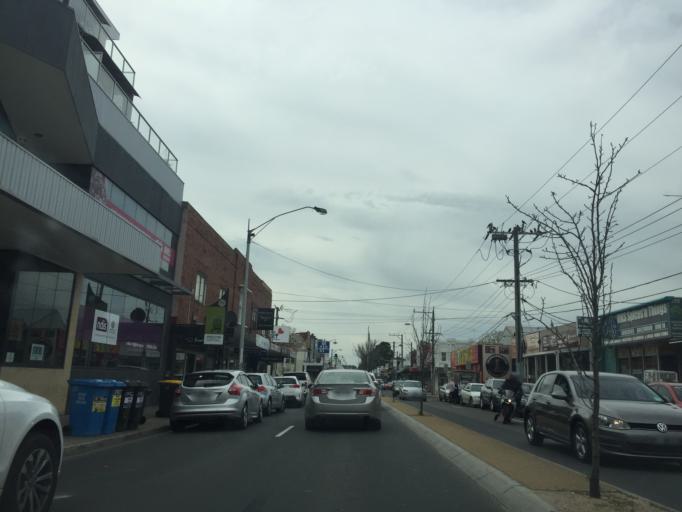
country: AU
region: Victoria
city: Thornbury
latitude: -37.7433
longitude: 145.0032
